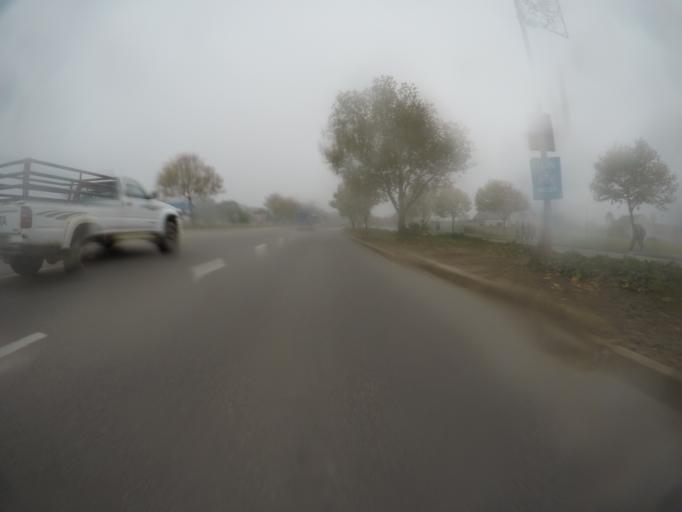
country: ZA
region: Western Cape
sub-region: Eden District Municipality
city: George
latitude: -33.9799
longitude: 22.4409
